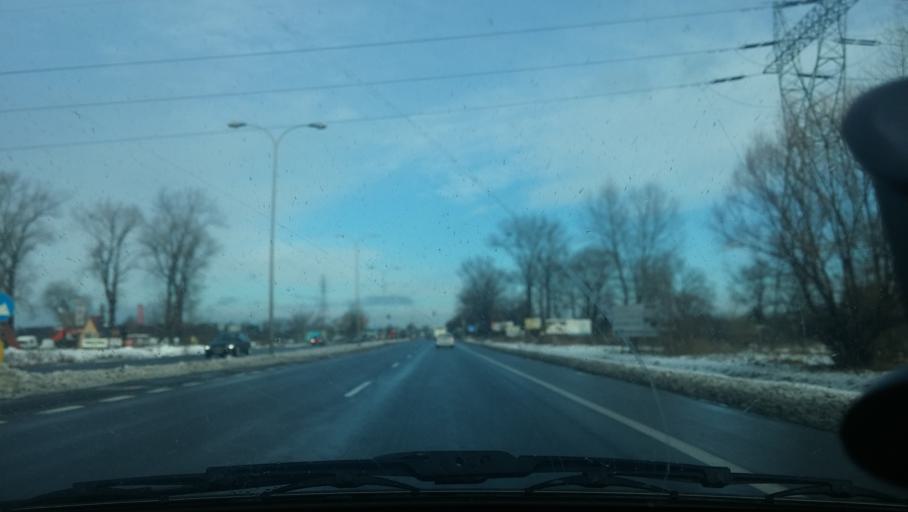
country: PL
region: Masovian Voivodeship
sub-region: Powiat wolominski
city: Zabki
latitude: 52.2925
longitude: 21.0800
